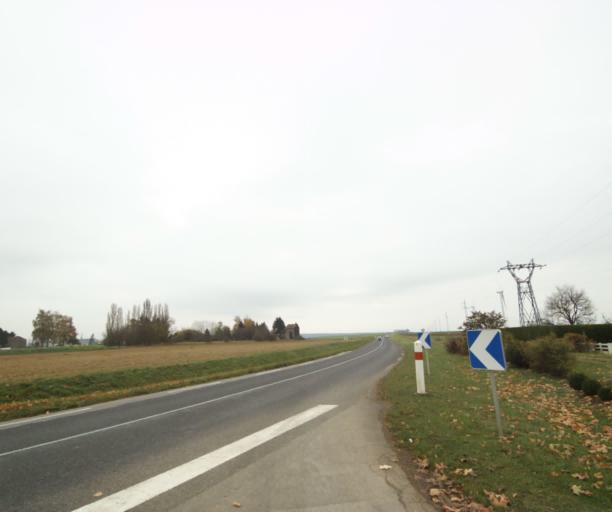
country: FR
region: Lorraine
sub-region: Departement de Meurthe-et-Moselle
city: Mancieulles
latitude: 49.2774
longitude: 5.8760
